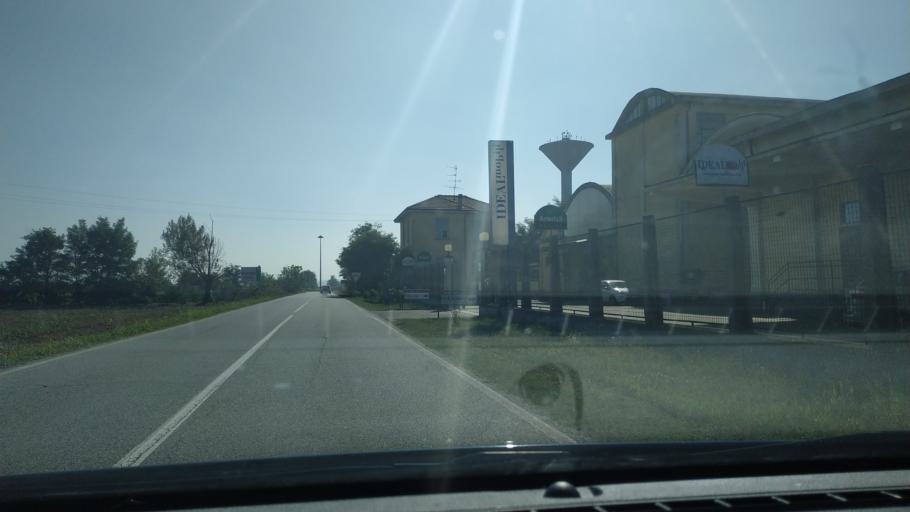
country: IT
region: Piedmont
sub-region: Provincia di Alessandria
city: Borgo San Martino
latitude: 45.0964
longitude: 8.5352
